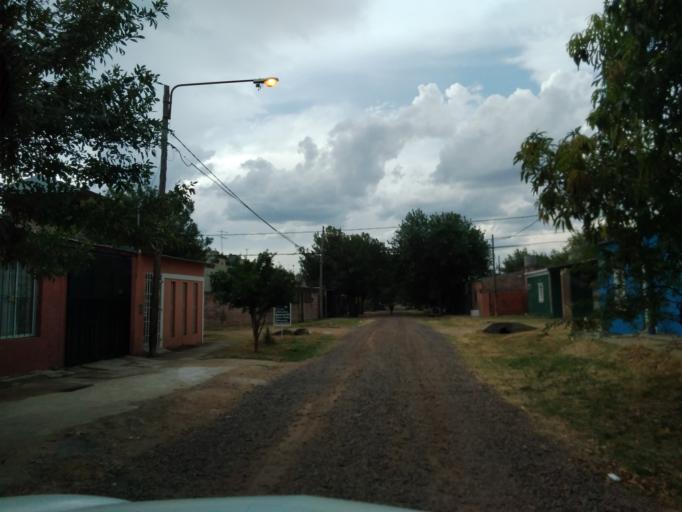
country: AR
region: Corrientes
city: Corrientes
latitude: -27.5207
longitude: -58.7901
